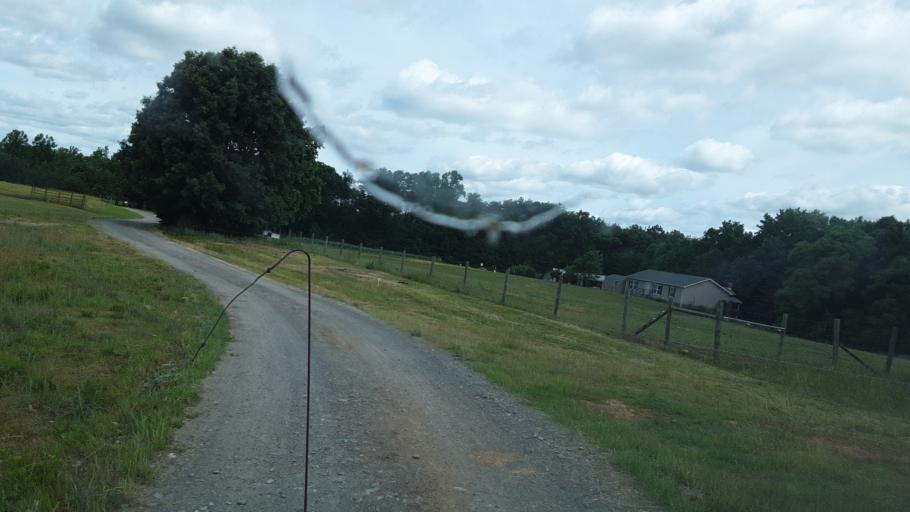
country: US
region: Virginia
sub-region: Pittsylvania County
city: Chatham
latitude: 36.8360
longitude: -79.4162
